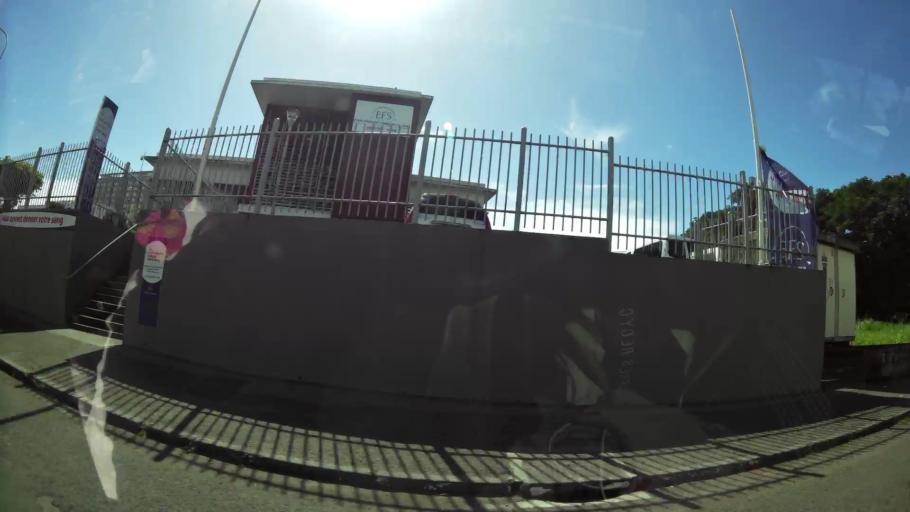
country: GP
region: Guadeloupe
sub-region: Guadeloupe
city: Pointe-a-Pitre
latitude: 16.2386
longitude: -61.5273
